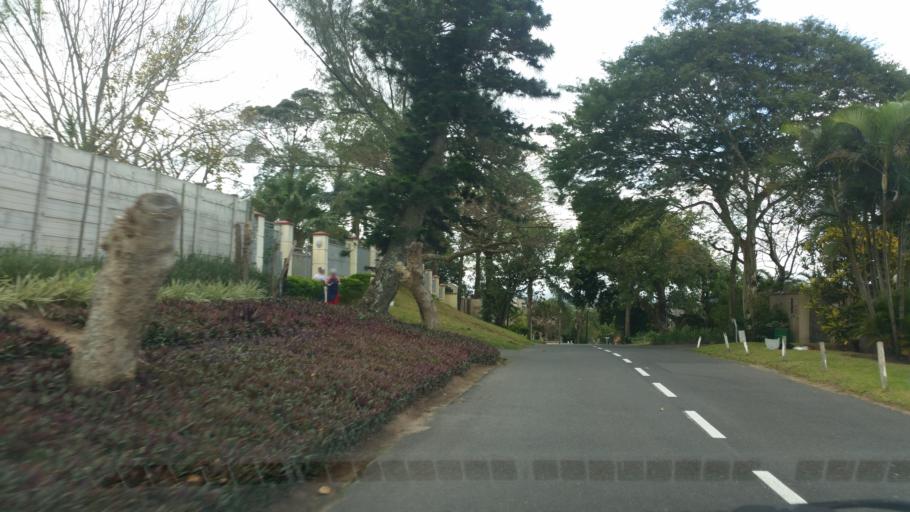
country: ZA
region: KwaZulu-Natal
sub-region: eThekwini Metropolitan Municipality
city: Berea
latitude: -29.8251
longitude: 30.9391
